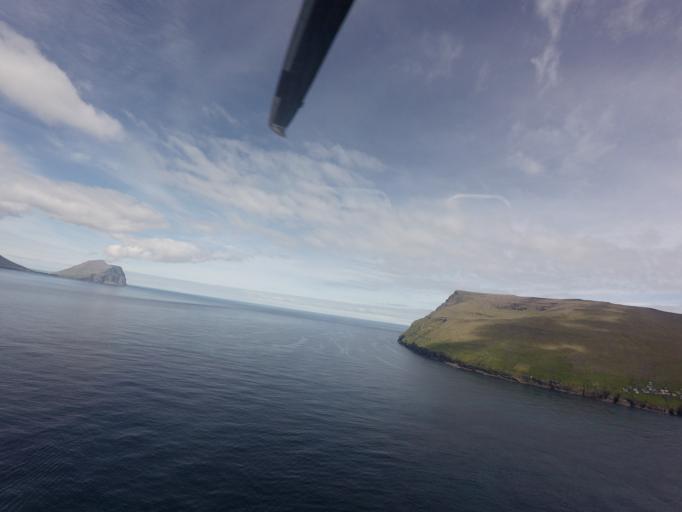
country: FO
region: Nordoyar
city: Klaksvik
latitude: 62.3077
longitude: -6.3321
